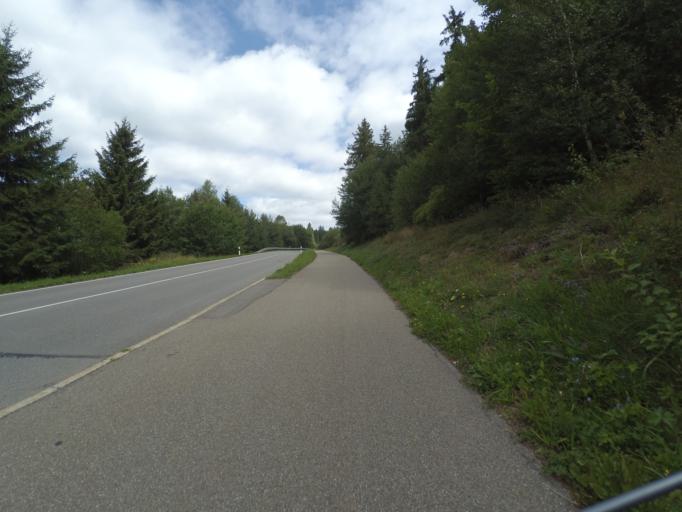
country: DE
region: Baden-Wuerttemberg
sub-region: Freiburg Region
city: Schluchsee
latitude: 47.8225
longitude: 8.1837
